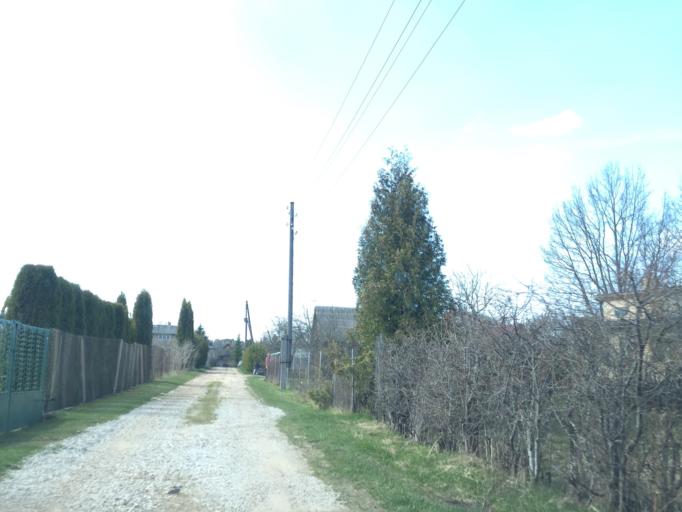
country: LV
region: Saulkrastu
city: Saulkrasti
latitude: 57.2384
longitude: 24.4536
